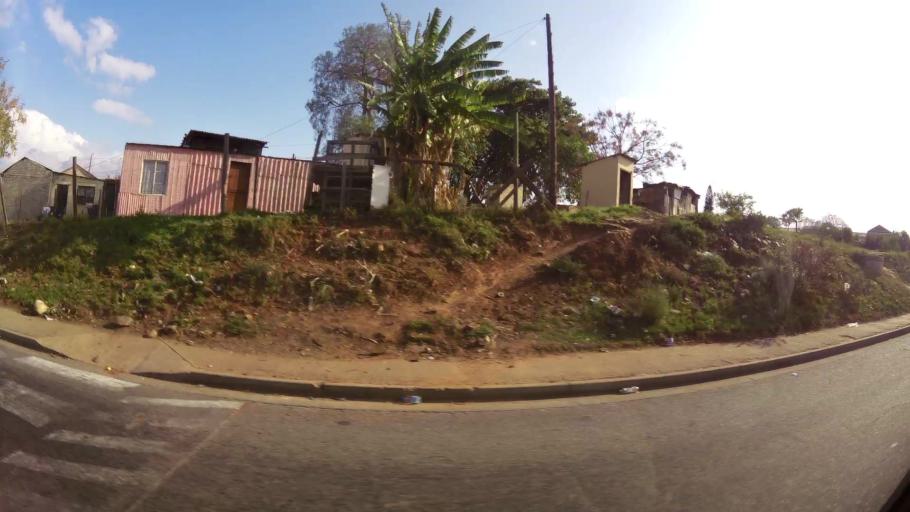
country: ZA
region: Eastern Cape
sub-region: Nelson Mandela Bay Metropolitan Municipality
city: Uitenhage
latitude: -33.7546
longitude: 25.3875
